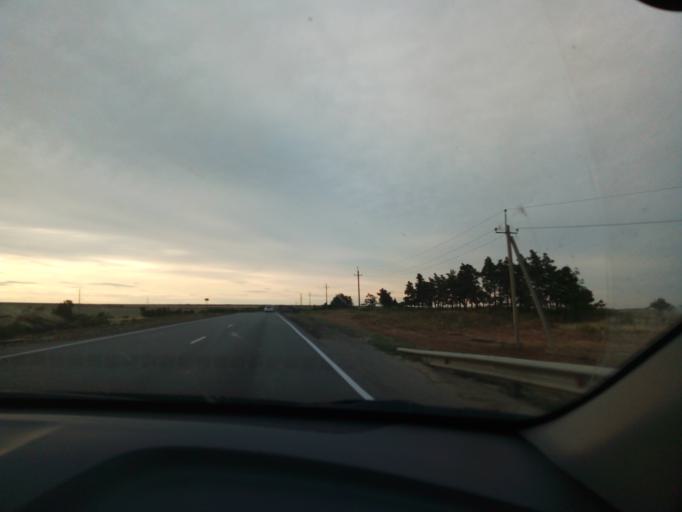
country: RU
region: Volgograd
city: Primorsk
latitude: 49.2535
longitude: 44.8872
